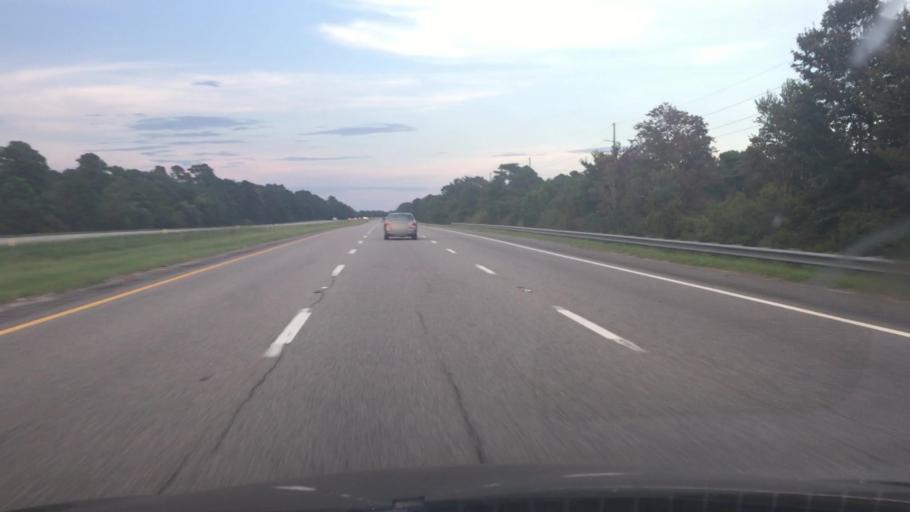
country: US
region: South Carolina
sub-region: Horry County
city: Forestbrook
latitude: 33.7462
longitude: -78.9155
